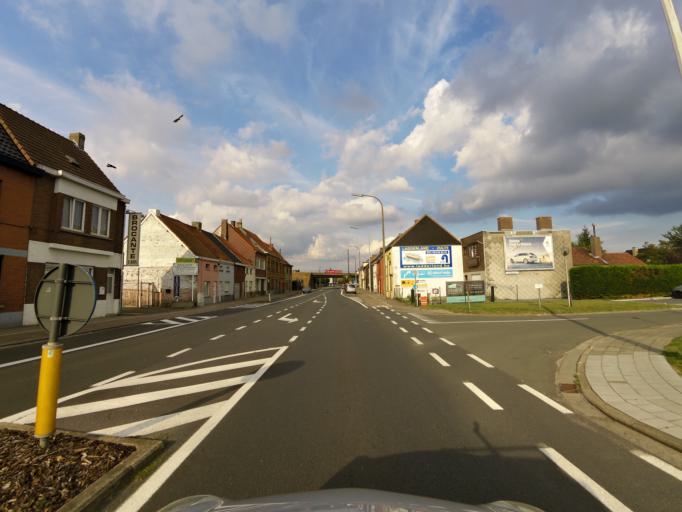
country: BE
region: Flanders
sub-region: Provincie Oost-Vlaanderen
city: Deinze
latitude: 50.9735
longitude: 3.5218
